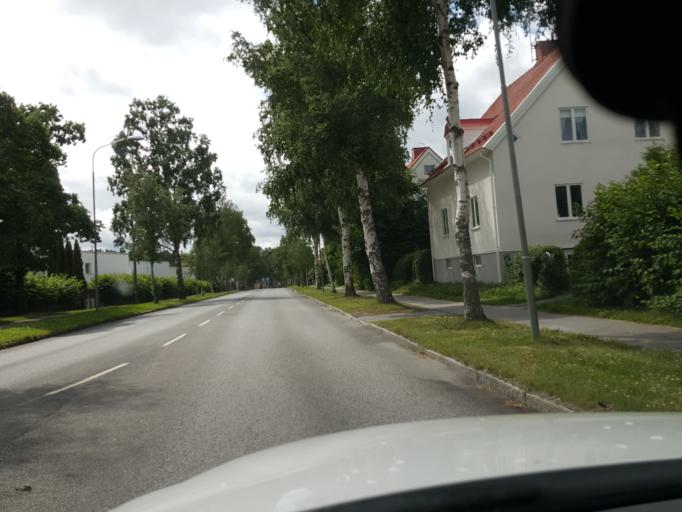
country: SE
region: Stockholm
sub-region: Stockholms Kommun
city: Bromma
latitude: 59.3210
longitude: 17.9716
